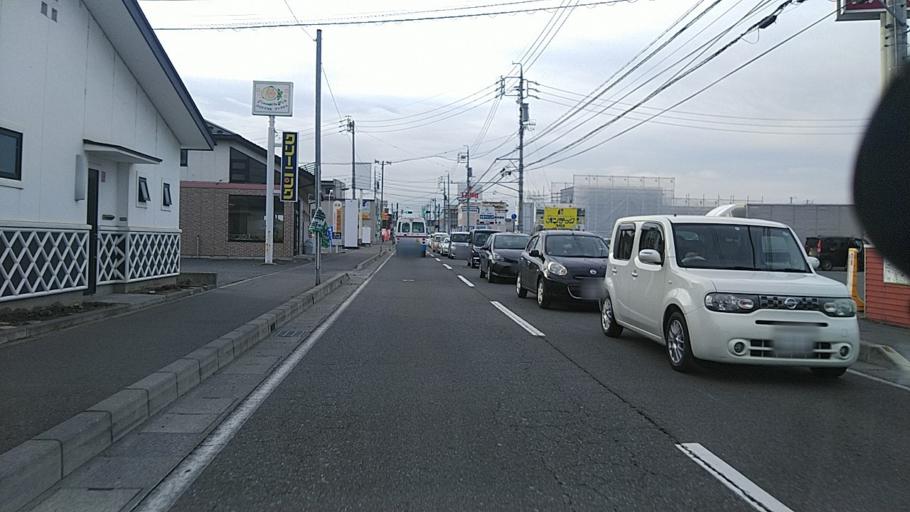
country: JP
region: Nagano
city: Matsumoto
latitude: 36.2112
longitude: 137.9795
